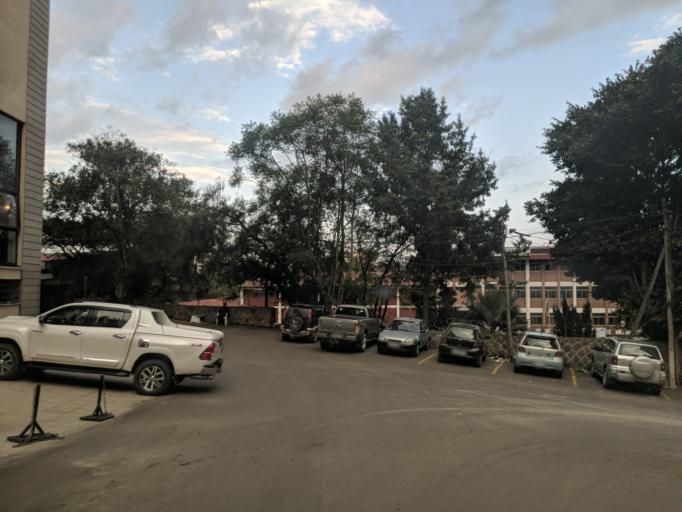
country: ET
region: Adis Abeba
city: Addis Ababa
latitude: 8.9877
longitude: 38.7715
